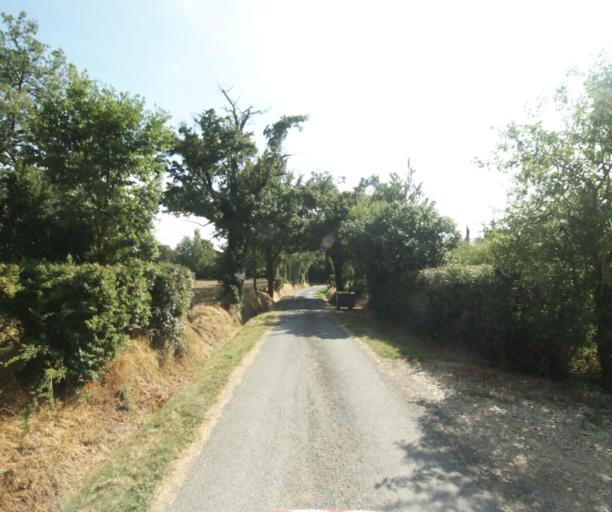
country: FR
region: Midi-Pyrenees
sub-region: Departement du Tarn
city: Puylaurens
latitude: 43.5277
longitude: 1.9799
